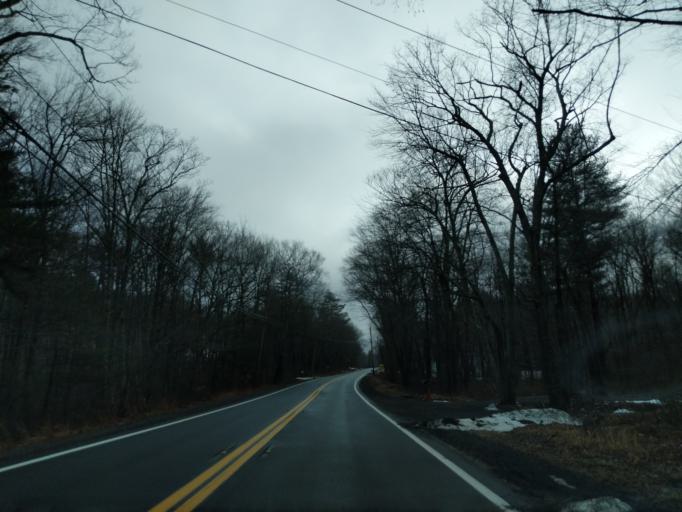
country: US
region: Massachusetts
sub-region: Worcester County
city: Douglas
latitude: 42.0547
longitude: -71.7574
